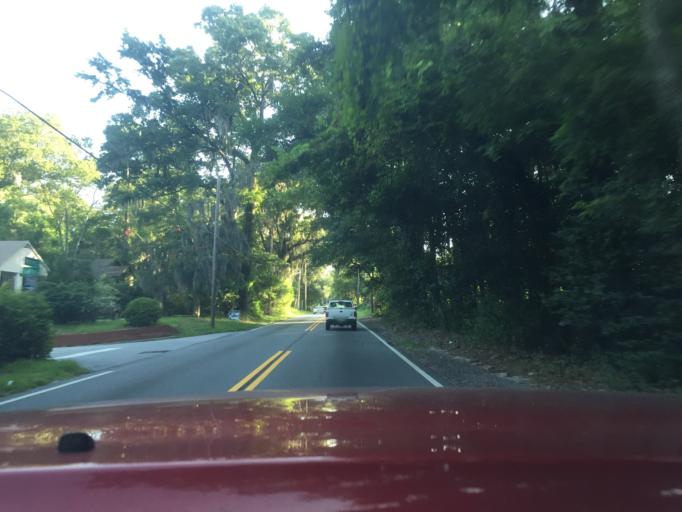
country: US
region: Georgia
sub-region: Chatham County
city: Isle of Hope
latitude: 32.0165
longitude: -81.0976
